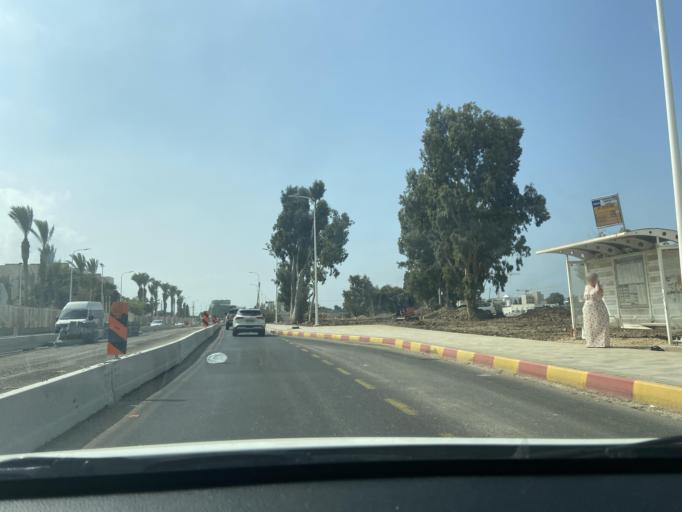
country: IL
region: Northern District
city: Nahariya
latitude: 33.0132
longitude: 35.1022
